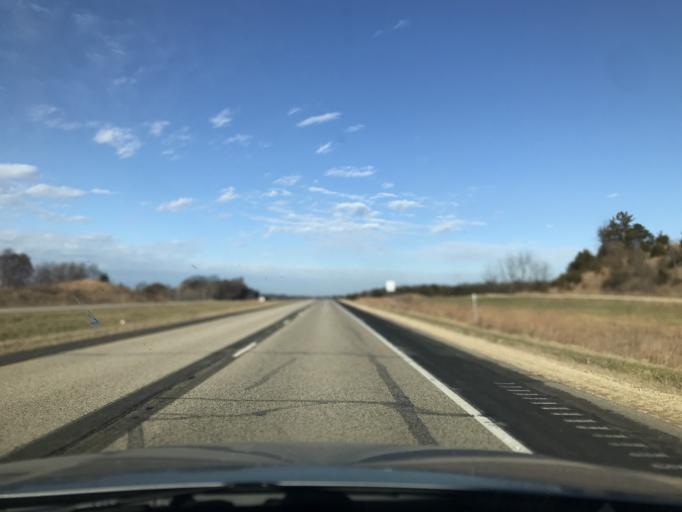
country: US
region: Iowa
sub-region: Jackson County
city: Maquoketa
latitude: 42.1365
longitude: -90.6759
